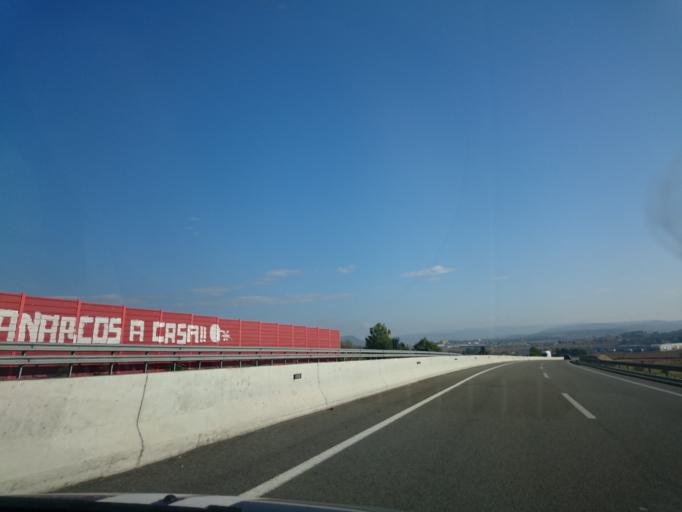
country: ES
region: Catalonia
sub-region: Provincia de Barcelona
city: Sant Fruitos de Bages
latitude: 41.7543
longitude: 1.8483
